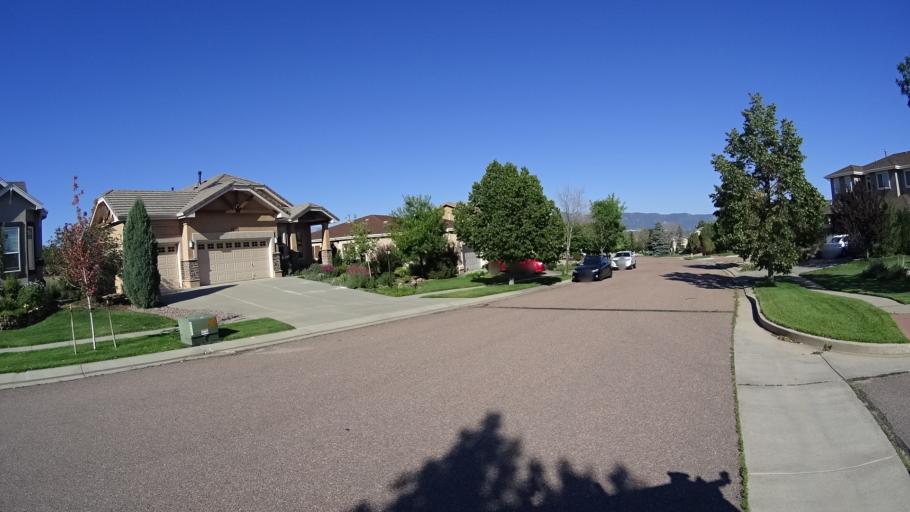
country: US
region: Colorado
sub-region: El Paso County
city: Black Forest
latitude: 38.9815
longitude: -104.7664
